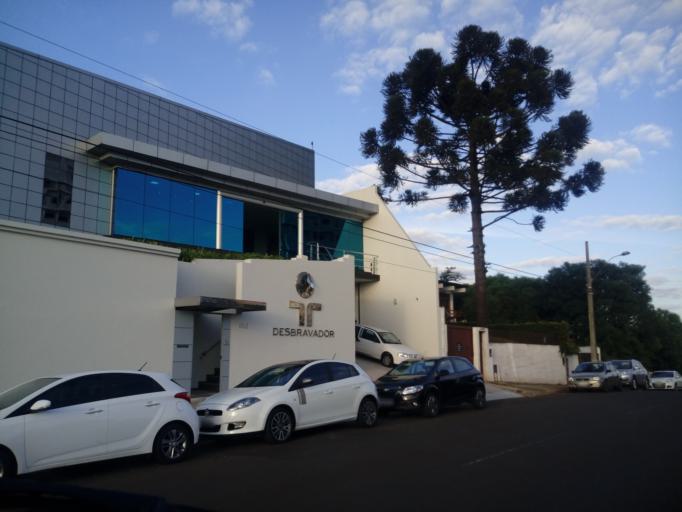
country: BR
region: Santa Catarina
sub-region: Chapeco
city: Chapeco
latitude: -27.1039
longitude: -52.6250
